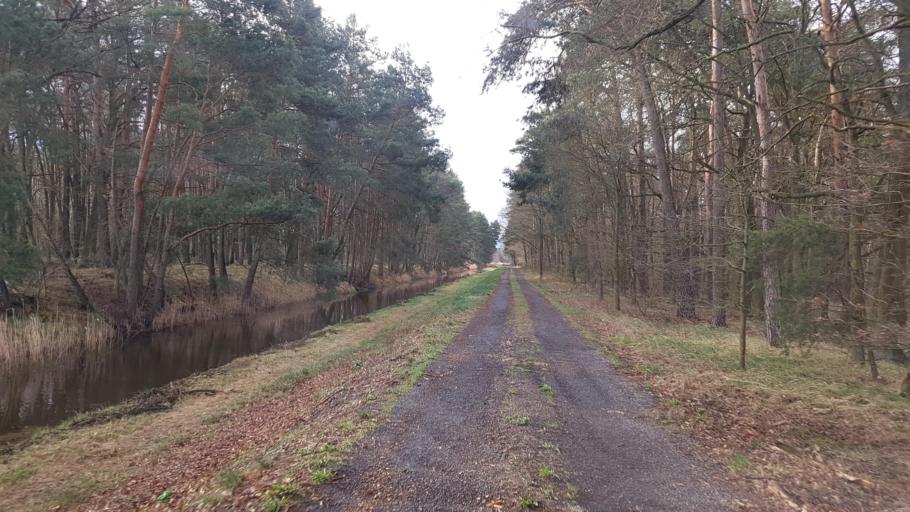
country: DE
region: Brandenburg
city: Bronkow
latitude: 51.6472
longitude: 13.8866
